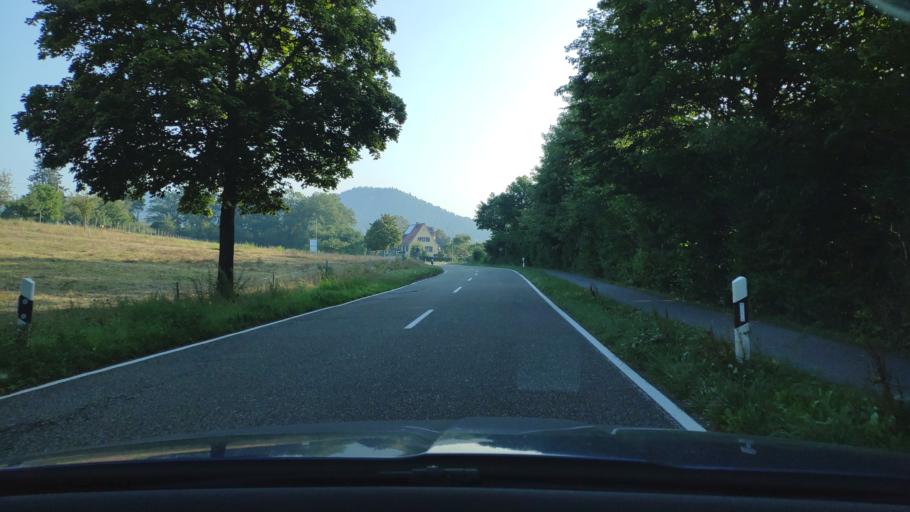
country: DE
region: Rheinland-Pfalz
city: Fischbach
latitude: 49.0794
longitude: 7.7116
